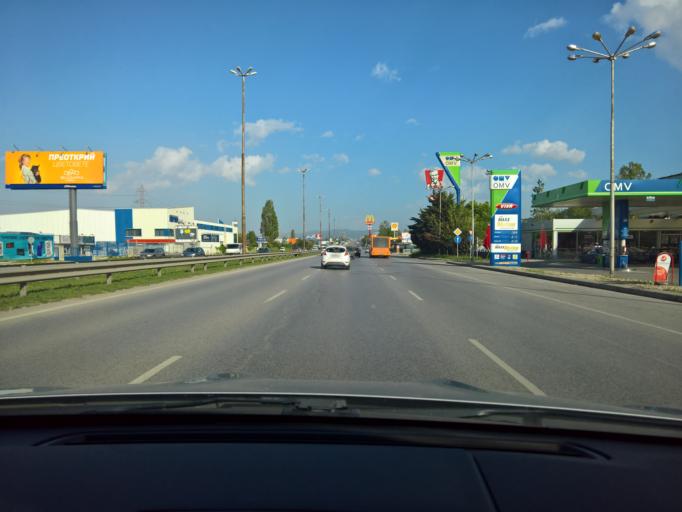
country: BG
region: Sofia-Capital
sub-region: Stolichna Obshtina
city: Sofia
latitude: 42.6514
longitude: 23.2885
